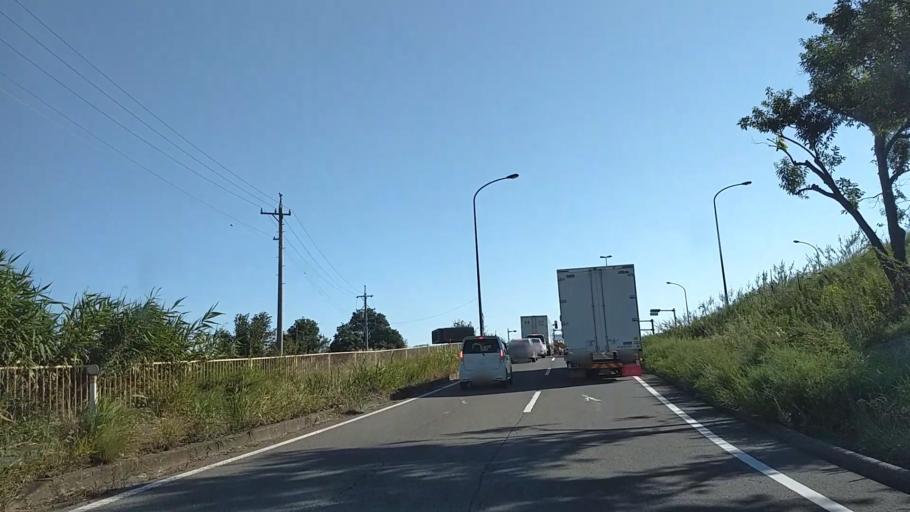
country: JP
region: Nagano
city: Nagano-shi
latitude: 36.5616
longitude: 138.1388
